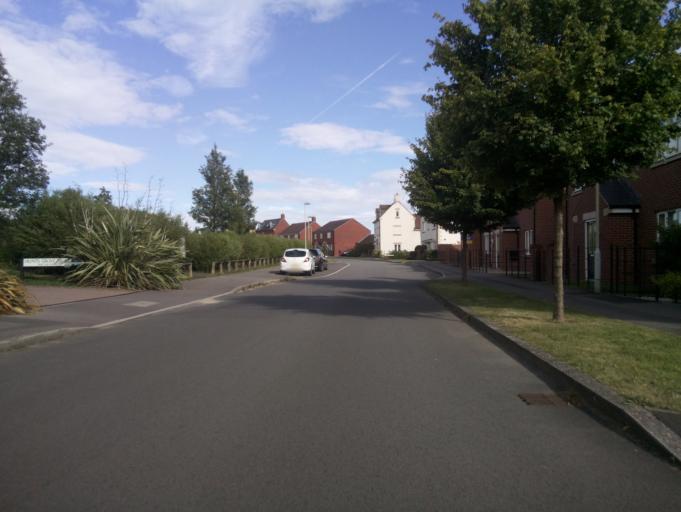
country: GB
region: England
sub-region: Gloucestershire
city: Stonehouse
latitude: 51.8095
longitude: -2.2718
